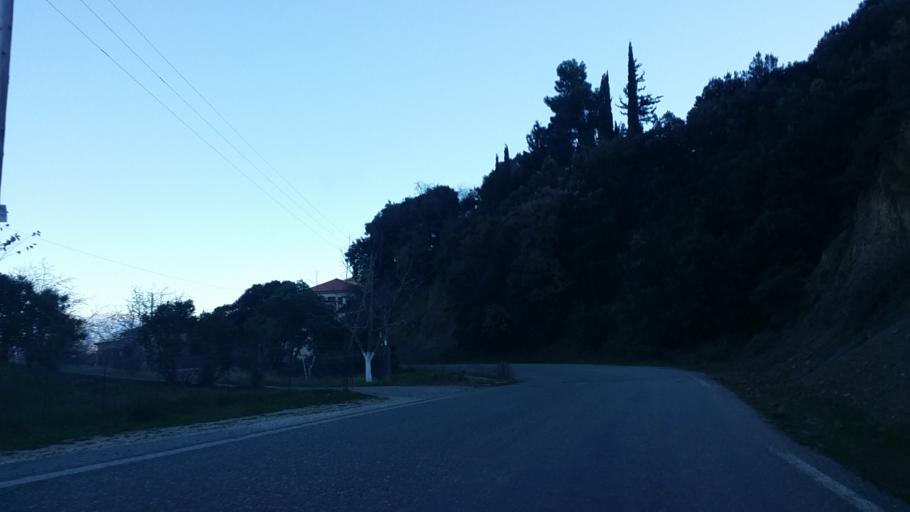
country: GR
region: West Greece
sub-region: Nomos Aitolias kai Akarnanias
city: Sardinia
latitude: 38.8700
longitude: 21.2841
